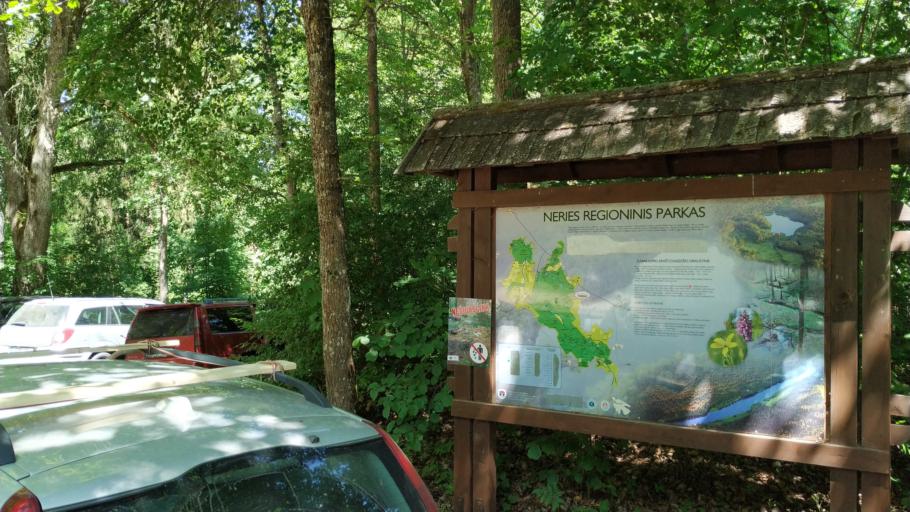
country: LT
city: Grigiskes
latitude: 54.7867
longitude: 24.9711
